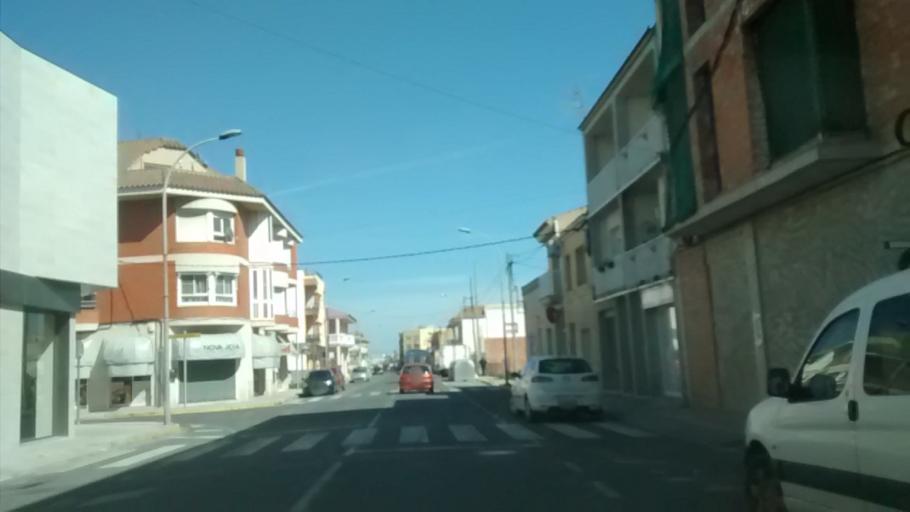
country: ES
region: Catalonia
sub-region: Provincia de Tarragona
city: Deltebre
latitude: 40.7185
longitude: 0.7224
